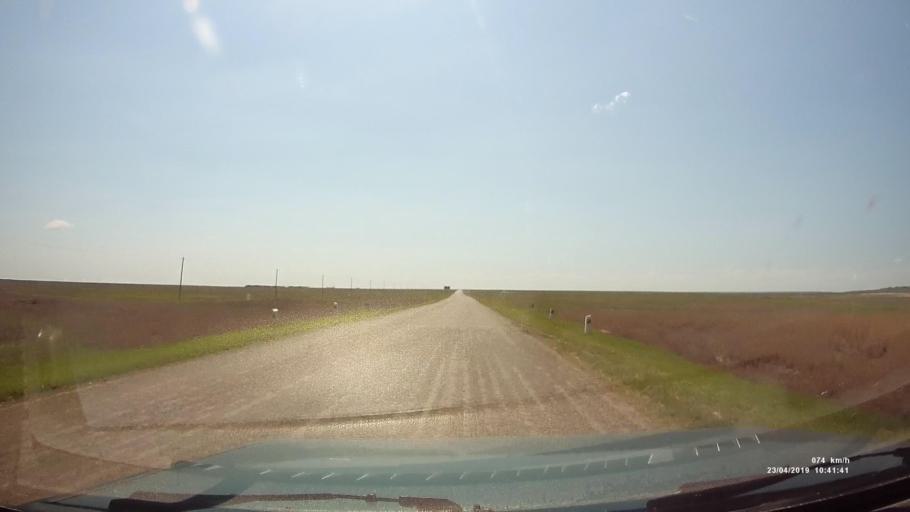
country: RU
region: Kalmykiya
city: Yashalta
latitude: 46.4913
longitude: 42.6384
